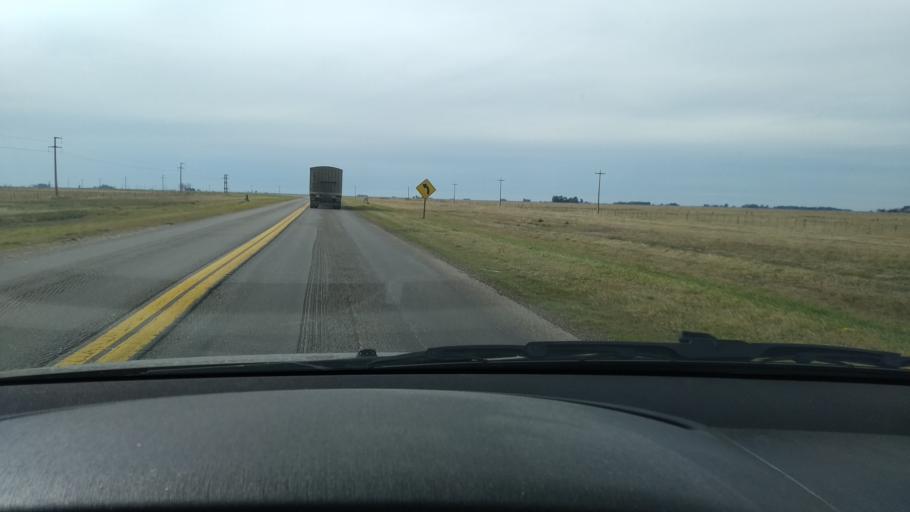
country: AR
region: Buenos Aires
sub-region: Partido de Azul
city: Azul
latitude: -36.7193
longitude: -59.7661
